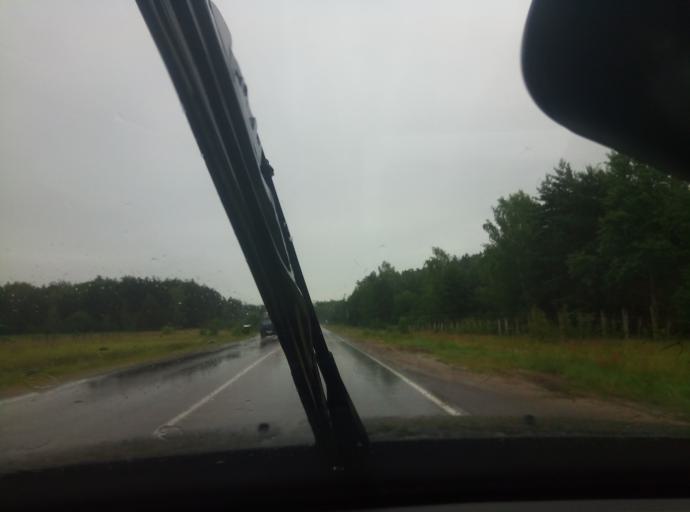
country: RU
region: Kaluga
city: Kremenki
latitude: 54.8779
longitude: 37.1411
